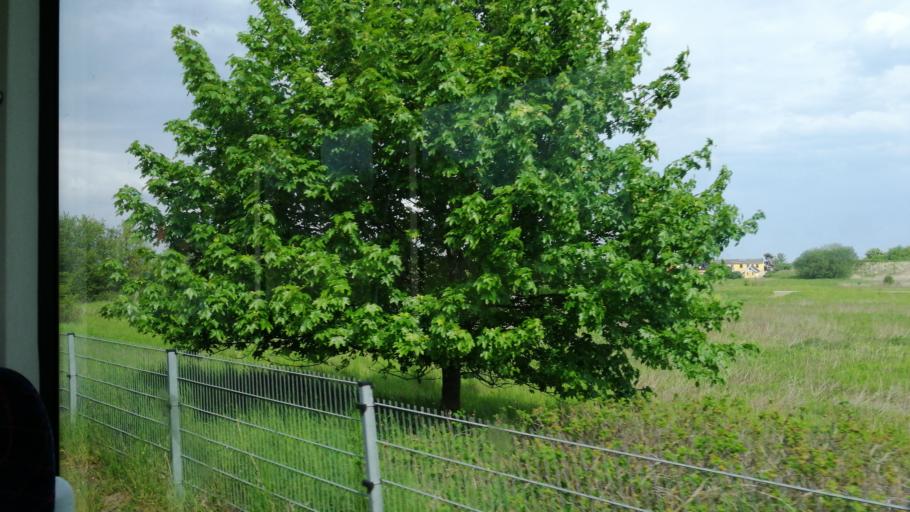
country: DK
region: Capital Region
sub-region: Helsingor Kommune
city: Hornbaek
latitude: 56.0963
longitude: 12.3993
